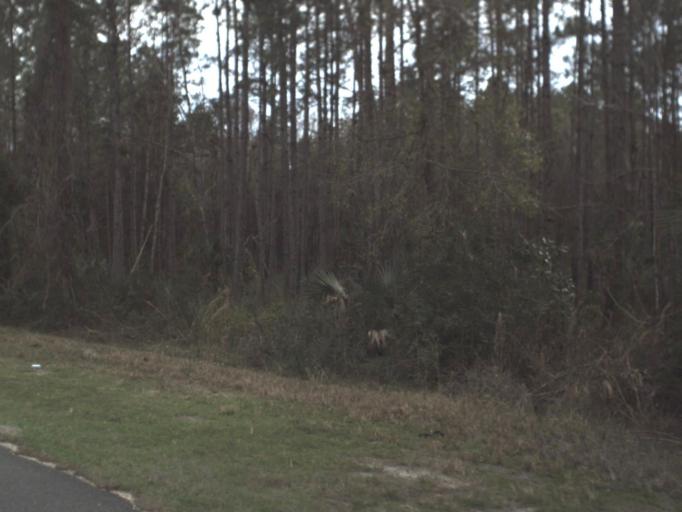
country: US
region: Florida
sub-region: Leon County
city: Woodville
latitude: 30.1662
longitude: -84.0054
